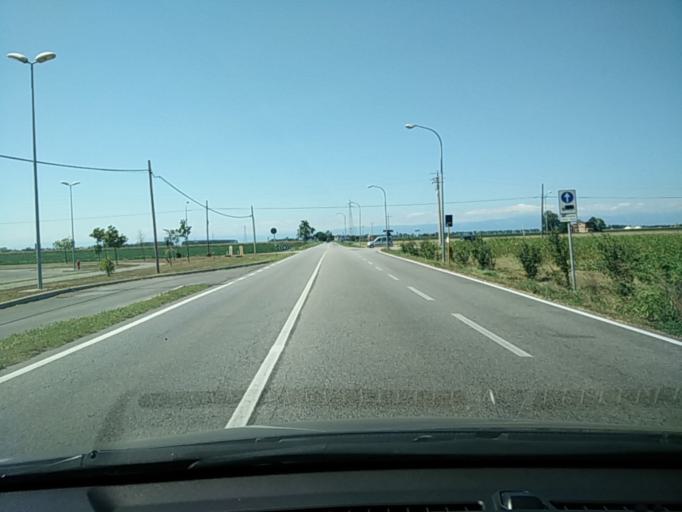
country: IT
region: Veneto
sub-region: Provincia di Venezia
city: La Salute di Livenza
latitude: 45.6542
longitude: 12.8317
